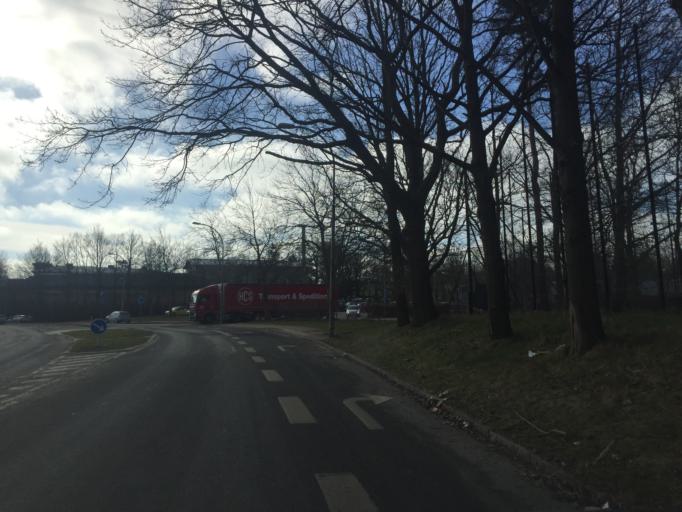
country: DK
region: Capital Region
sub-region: Lyngby-Tarbaek Kommune
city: Kongens Lyngby
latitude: 55.7577
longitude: 12.5246
